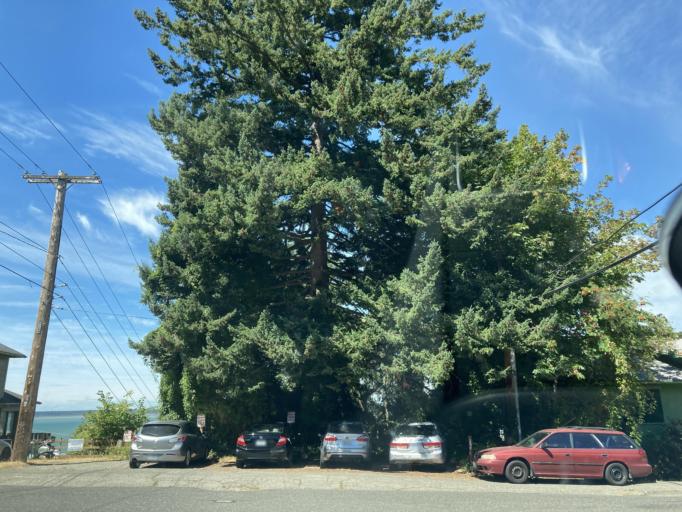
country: US
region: Washington
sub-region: Whatcom County
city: Bellingham
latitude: 48.7416
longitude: -122.4850
